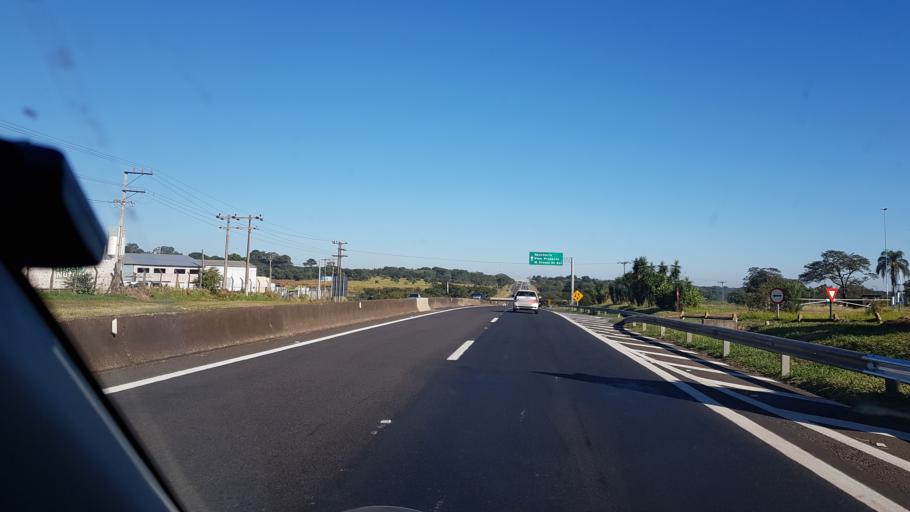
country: BR
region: Sao Paulo
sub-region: Assis
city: Assis
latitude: -22.6367
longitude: -50.4308
